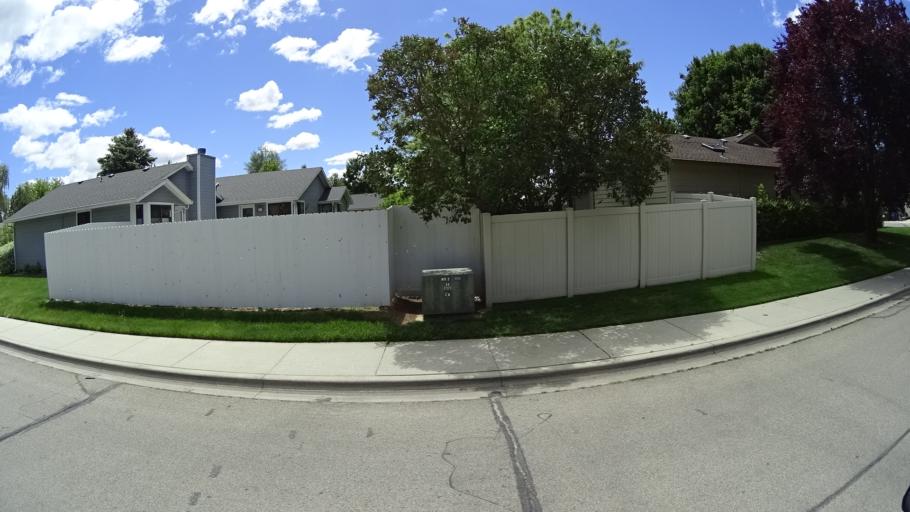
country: US
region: Idaho
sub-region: Ada County
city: Eagle
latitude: 43.6557
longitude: -116.3382
